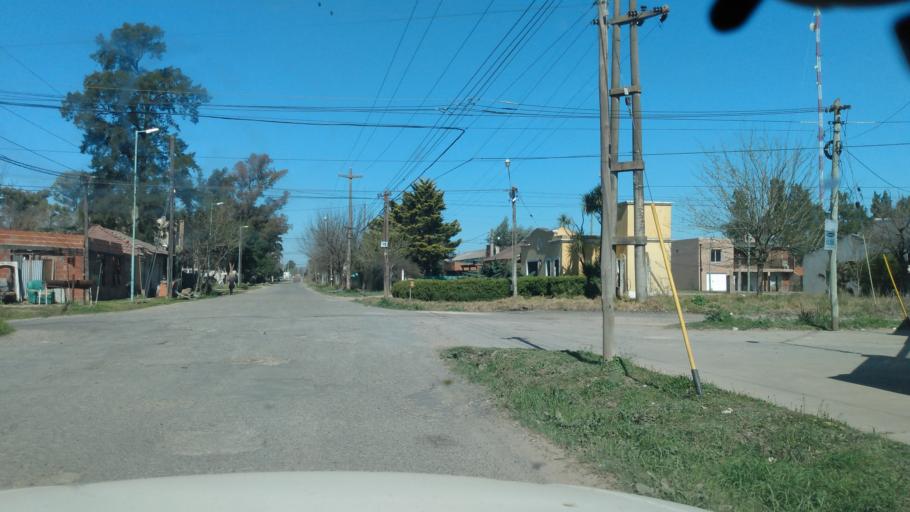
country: AR
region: Buenos Aires
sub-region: Partido de Lujan
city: Lujan
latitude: -34.5844
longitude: -59.1181
